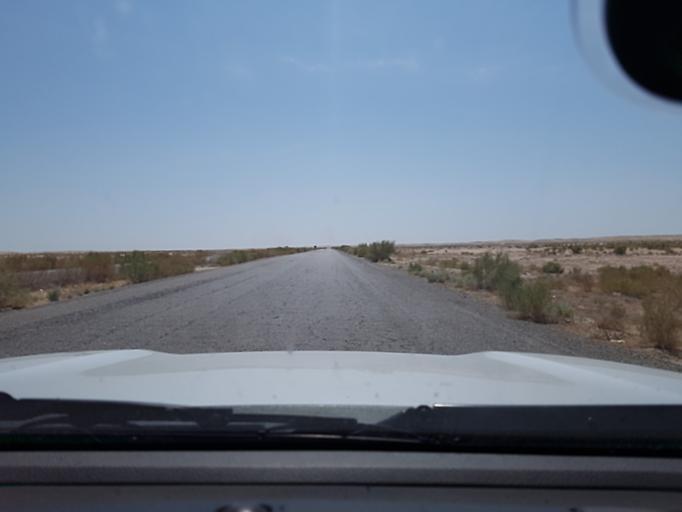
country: TM
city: Akdepe
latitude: 41.4143
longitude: 58.5450
